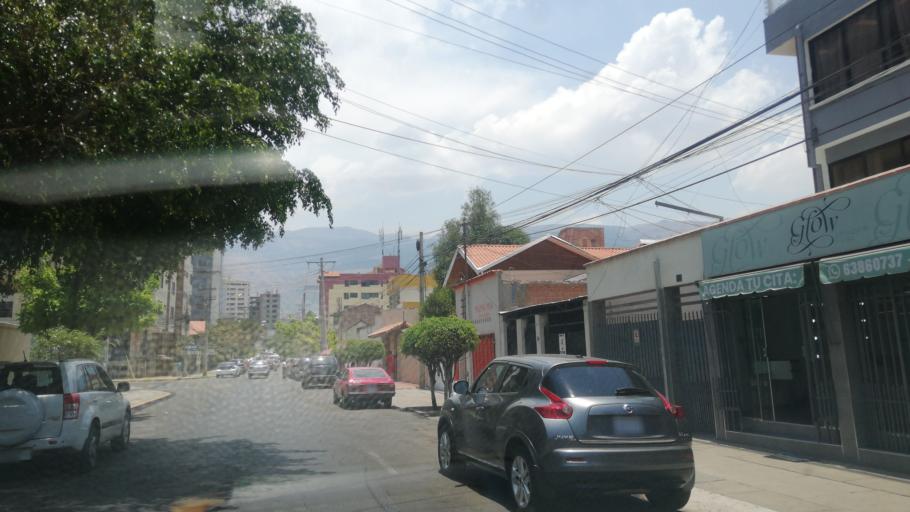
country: BO
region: Cochabamba
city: Cochabamba
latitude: -17.3764
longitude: -66.1609
